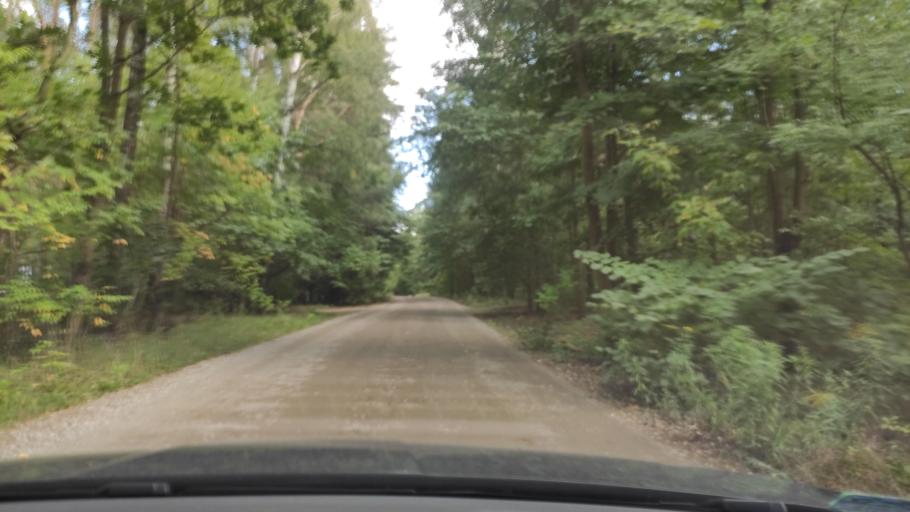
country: PL
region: Greater Poland Voivodeship
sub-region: Powiat poznanski
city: Swarzedz
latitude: 52.4159
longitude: 17.0380
